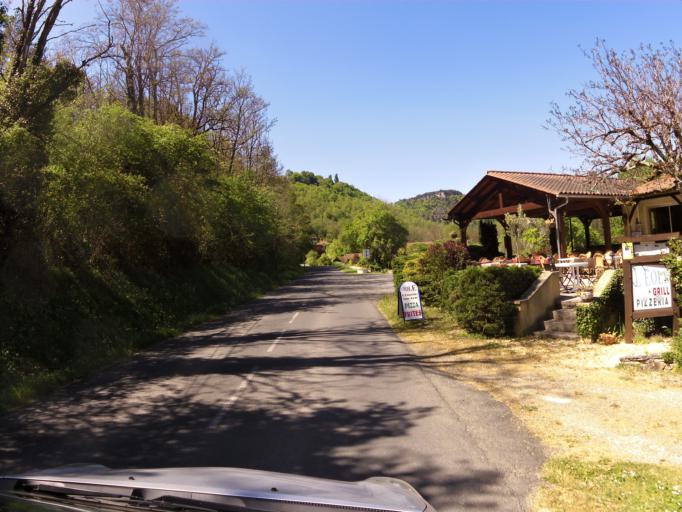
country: FR
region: Aquitaine
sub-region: Departement de la Dordogne
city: Cenac-et-Saint-Julien
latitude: 44.7891
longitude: 1.1644
